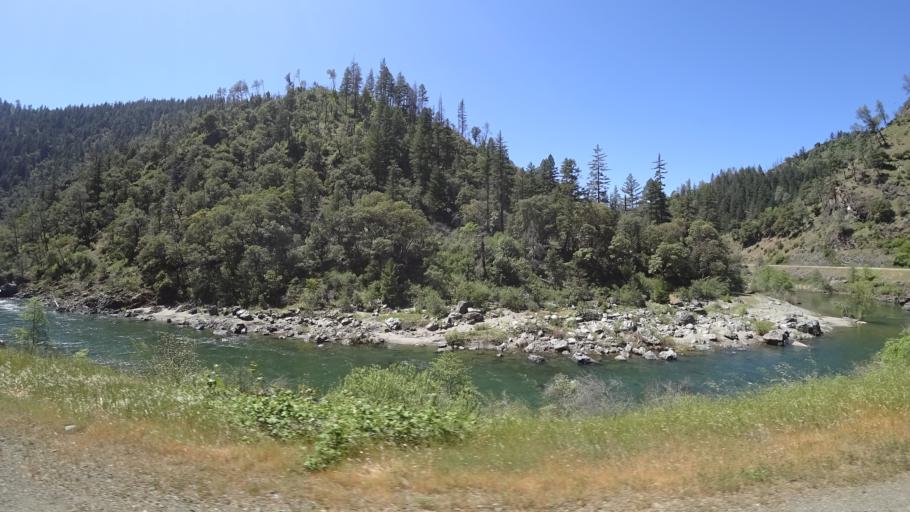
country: US
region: California
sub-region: Trinity County
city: Hayfork
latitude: 40.7600
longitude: -123.2816
